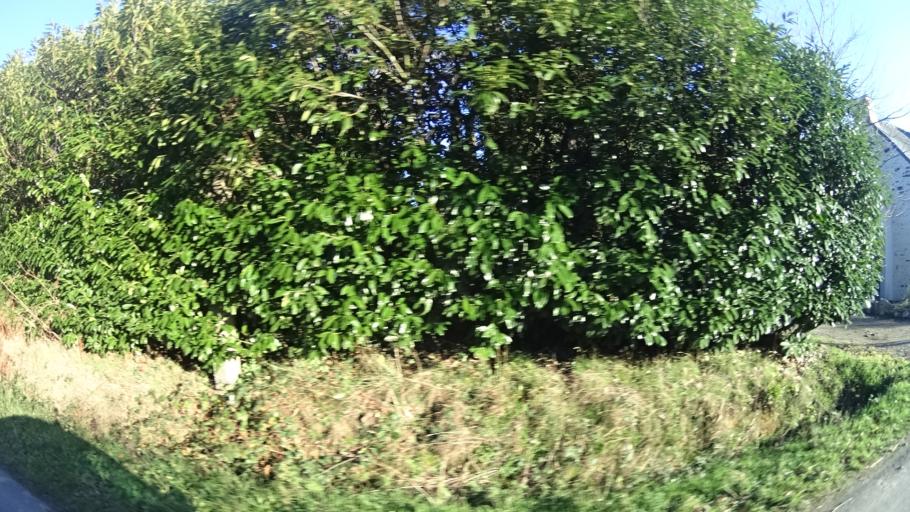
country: FR
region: Brittany
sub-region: Departement du Morbihan
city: Saint-Jacut-les-Pins
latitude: 47.6684
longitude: -2.1936
